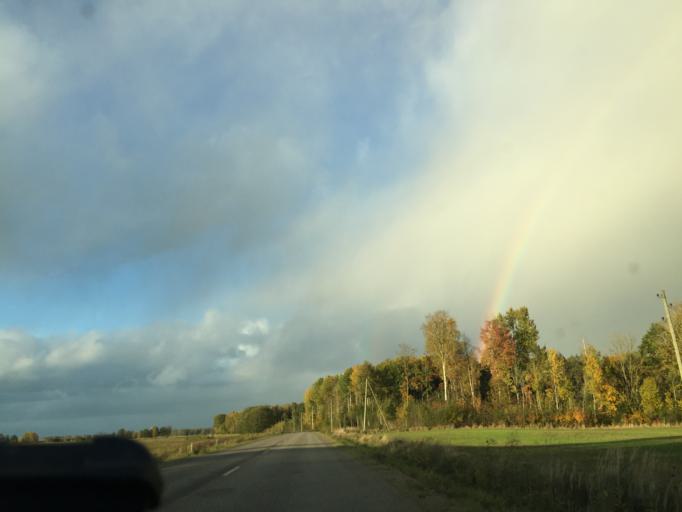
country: LV
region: Broceni
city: Broceni
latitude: 56.8654
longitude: 22.3825
